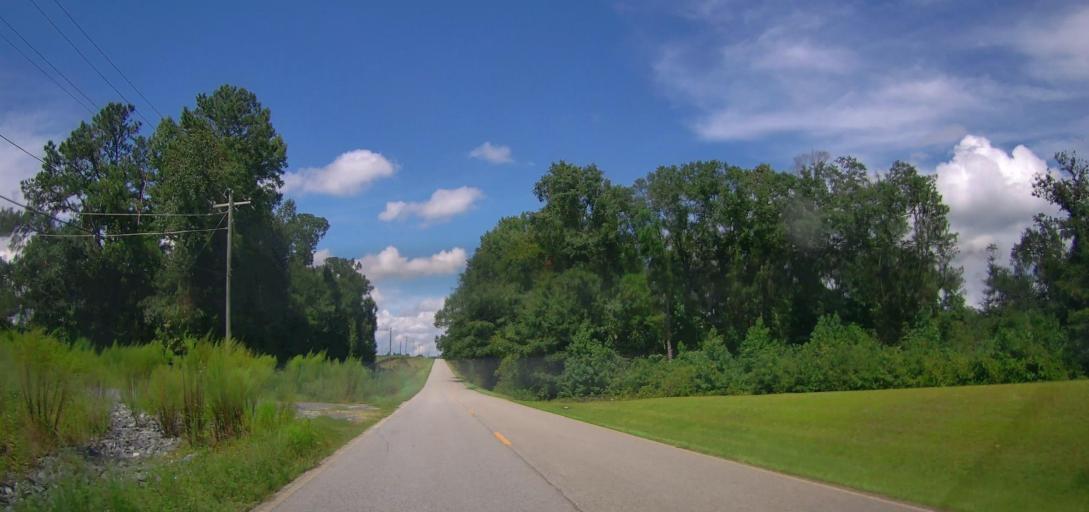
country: US
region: Georgia
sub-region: Peach County
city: Fort Valley
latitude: 32.5058
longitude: -83.8648
